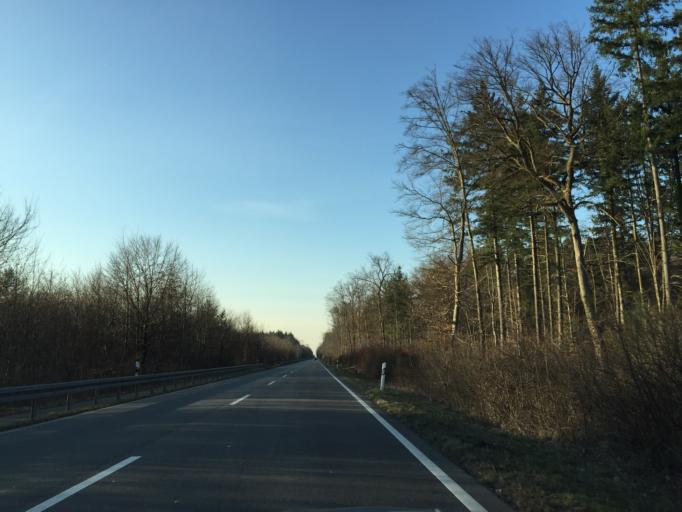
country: DE
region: Baden-Wuerttemberg
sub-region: Karlsruhe Region
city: Walldorf
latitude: 49.3291
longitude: 8.6200
